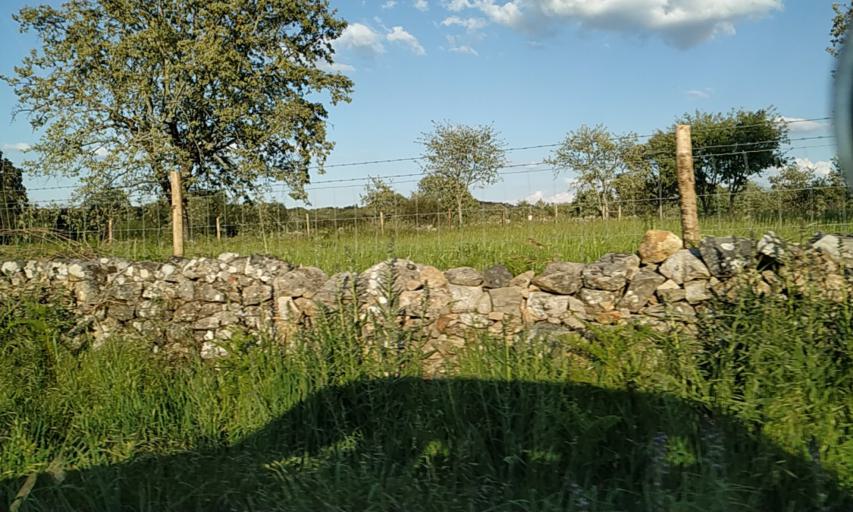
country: PT
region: Portalegre
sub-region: Portalegre
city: Reguengo
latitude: 39.3442
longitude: -7.4092
